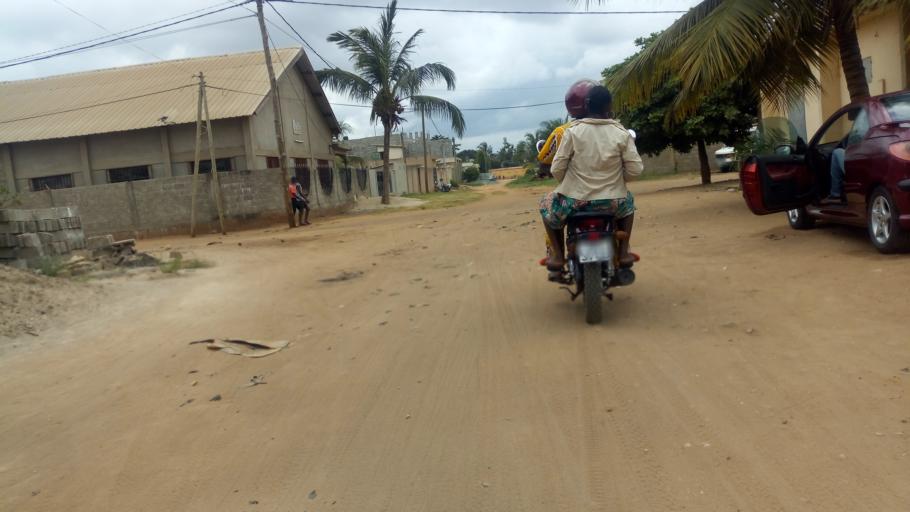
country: TG
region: Maritime
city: Lome
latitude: 6.2268
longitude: 1.1890
